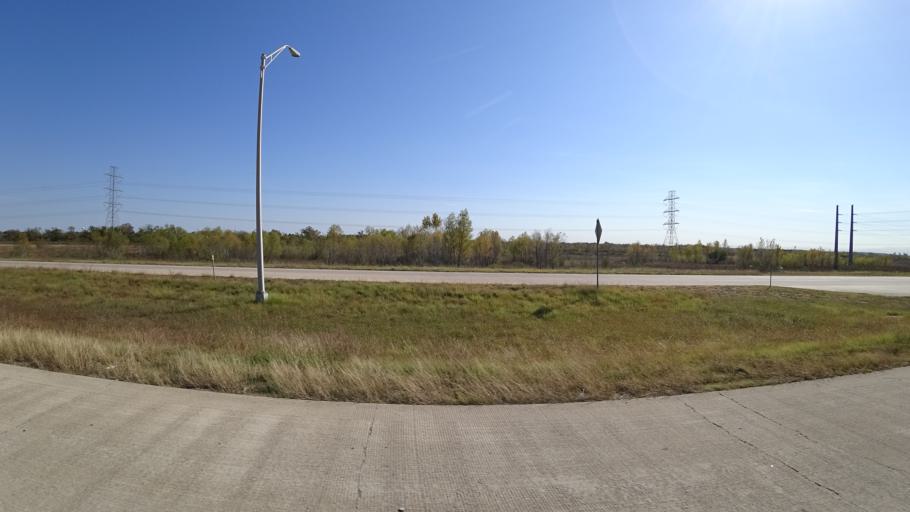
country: US
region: Texas
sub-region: Travis County
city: Hornsby Bend
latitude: 30.2466
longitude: -97.6088
